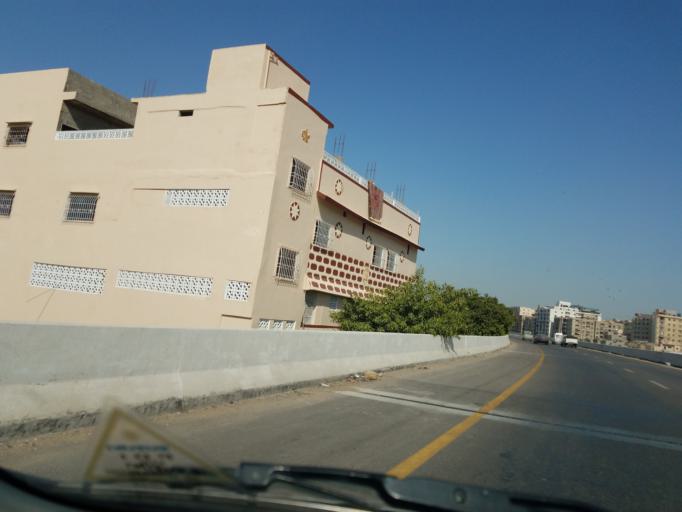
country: PK
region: Sindh
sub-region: Karachi District
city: Karachi
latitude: 24.8798
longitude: 67.0148
